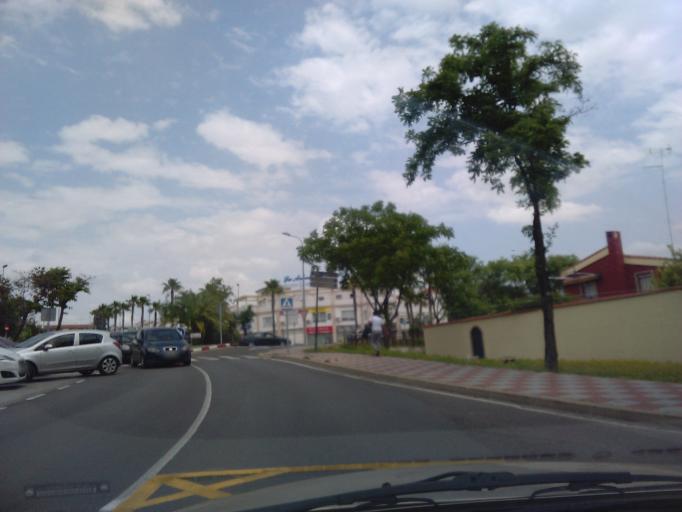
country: ES
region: Andalusia
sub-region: Provincia de Sevilla
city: Tomares
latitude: 37.3717
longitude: -6.0393
